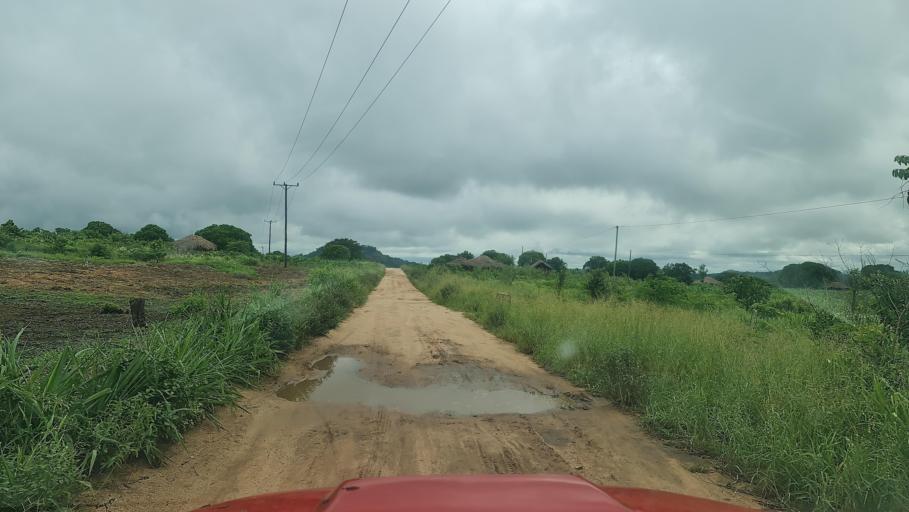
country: MW
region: Southern Region
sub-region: Nsanje District
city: Nsanje
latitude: -17.1840
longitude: 35.9265
